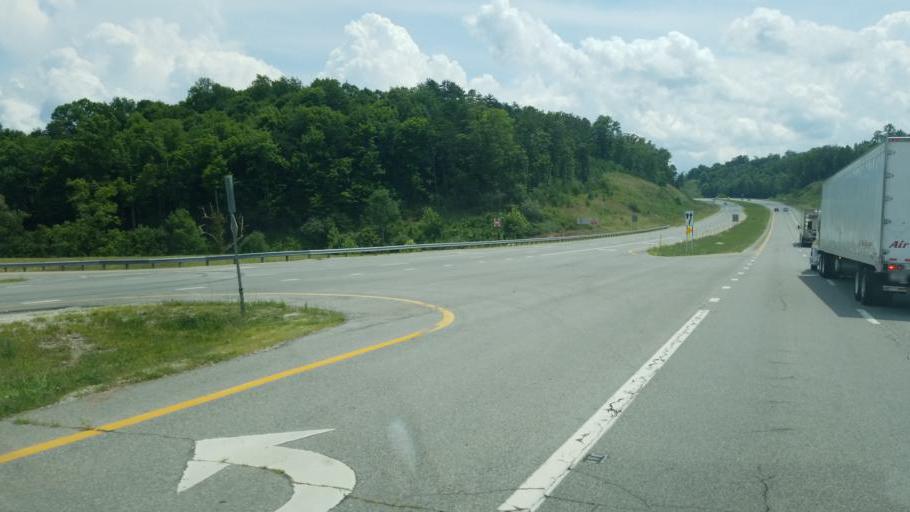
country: US
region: West Virginia
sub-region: Putnam County
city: Buffalo
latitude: 38.5686
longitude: -82.0138
